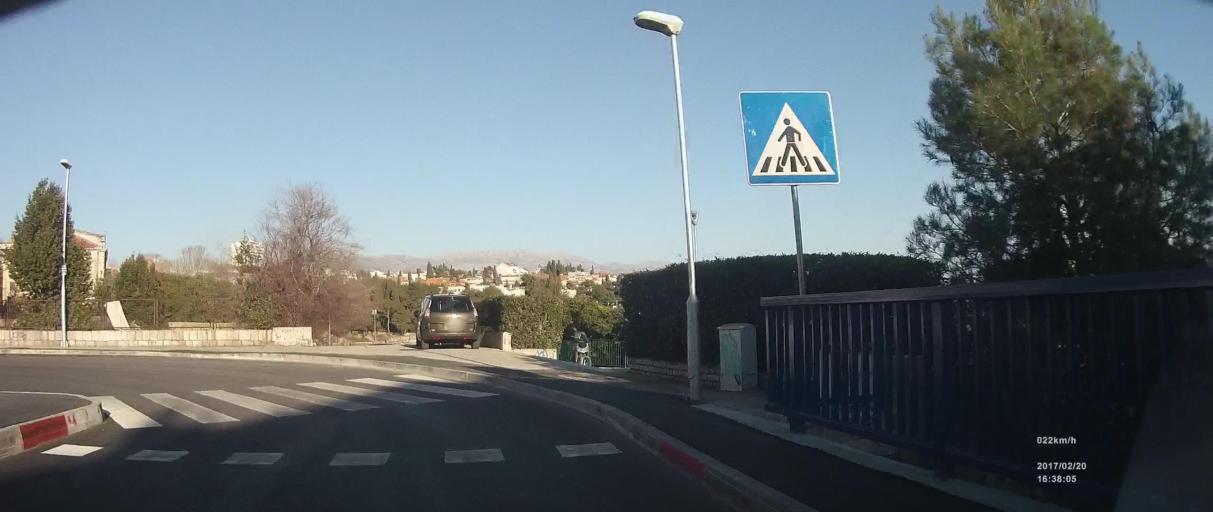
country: HR
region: Splitsko-Dalmatinska
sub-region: Grad Split
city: Split
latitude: 43.5015
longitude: 16.4450
